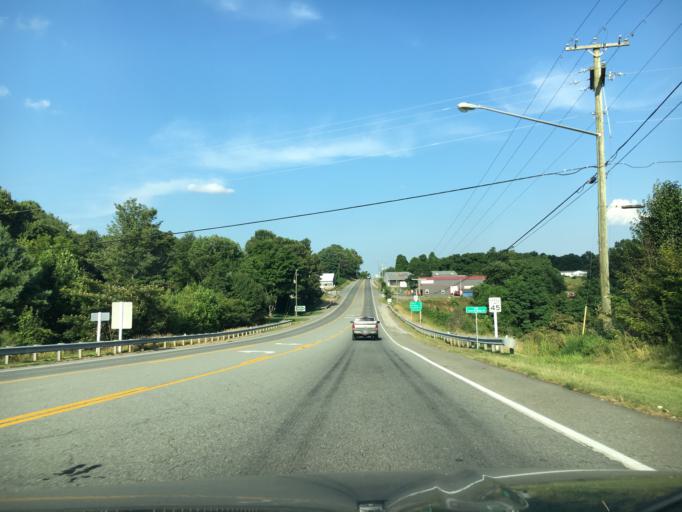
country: US
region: Virginia
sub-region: Franklin County
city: Rocky Mount
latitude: 37.0179
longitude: -79.8561
